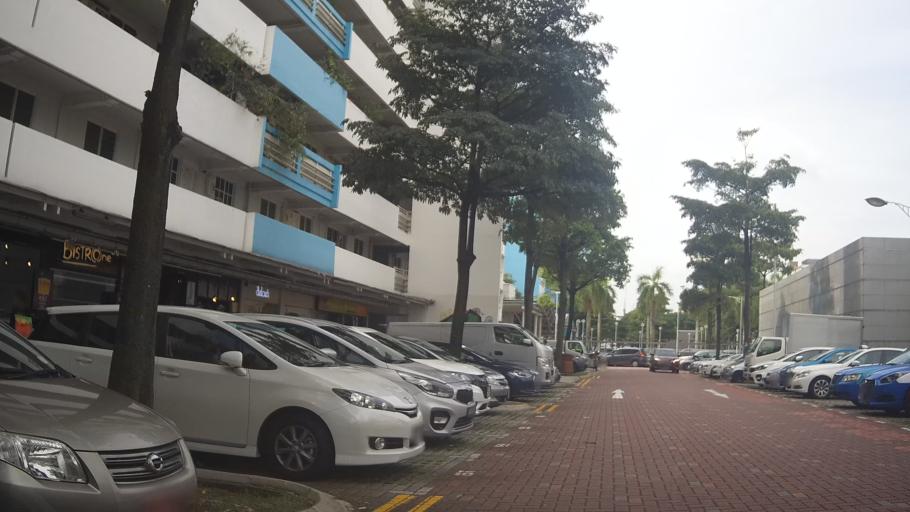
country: SG
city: Singapore
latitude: 1.3202
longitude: 103.8625
